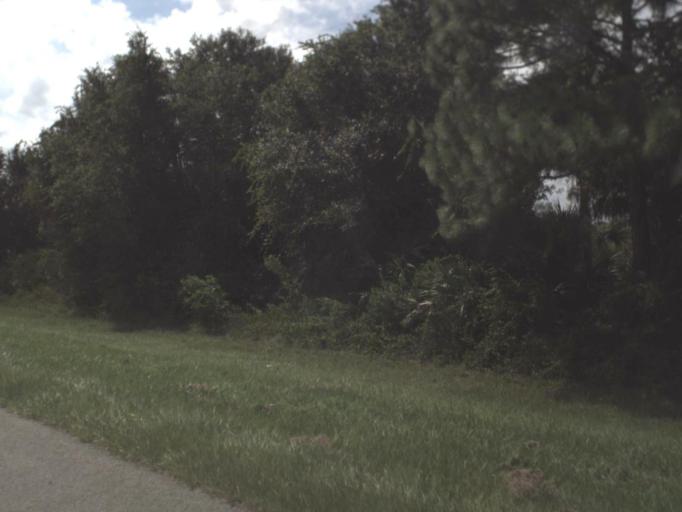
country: US
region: Florida
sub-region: Collier County
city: Immokalee
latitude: 26.3505
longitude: -81.3437
